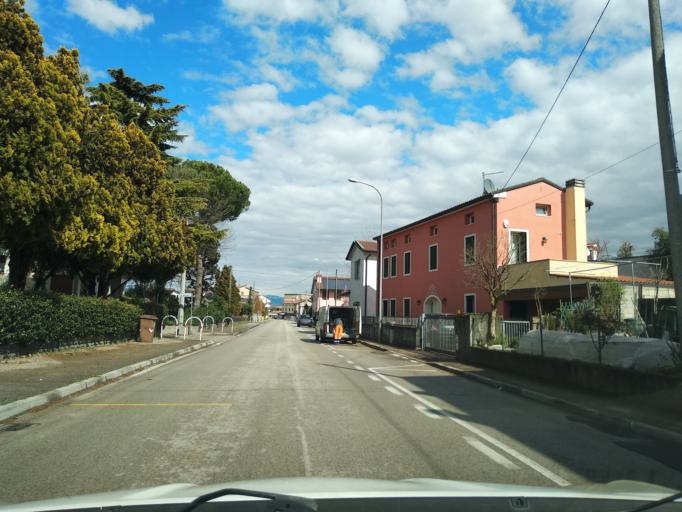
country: IT
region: Veneto
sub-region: Provincia di Vicenza
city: Vigardolo
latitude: 45.6037
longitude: 11.5905
